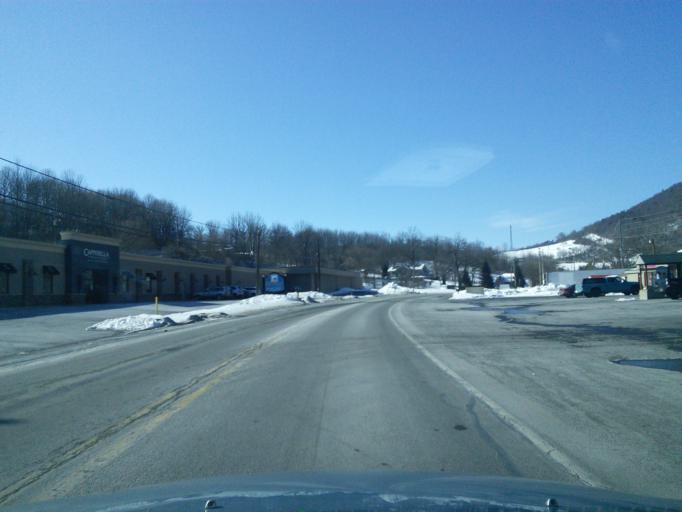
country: US
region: Pennsylvania
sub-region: Centre County
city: Bellefonte
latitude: 40.9237
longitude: -77.7800
